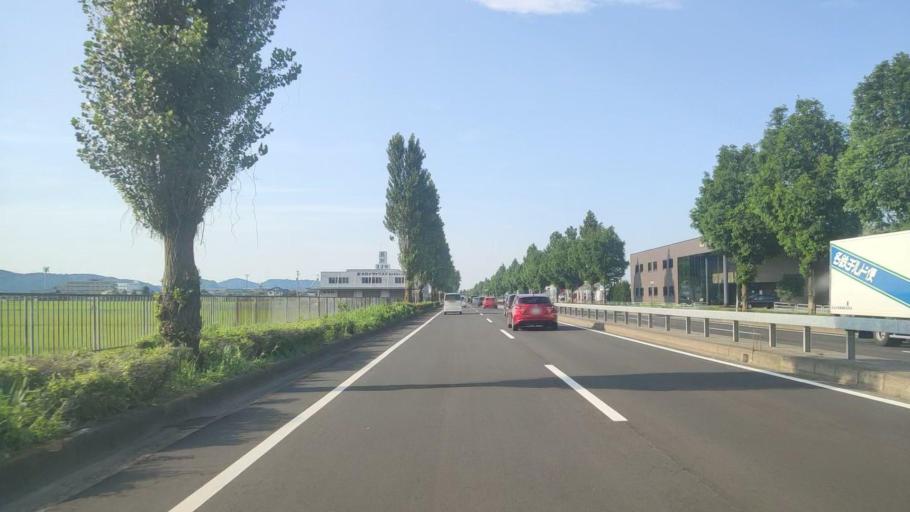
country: JP
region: Fukui
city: Sabae
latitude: 35.9987
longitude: 136.2067
